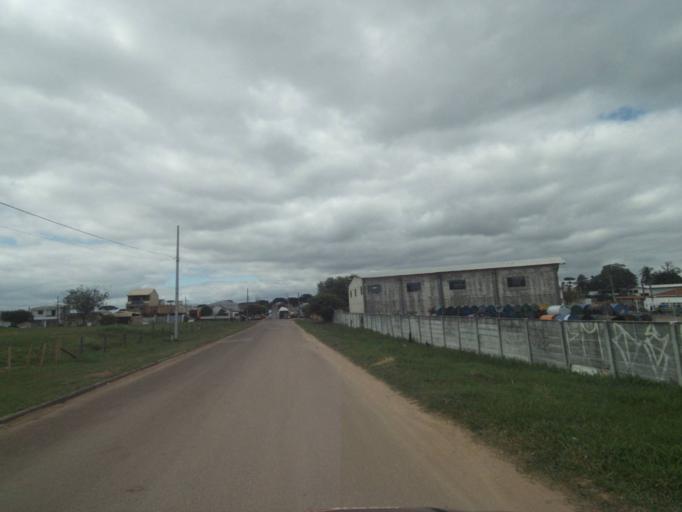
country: BR
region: Parana
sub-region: Sao Jose Dos Pinhais
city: Sao Jose dos Pinhais
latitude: -25.5599
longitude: -49.2639
